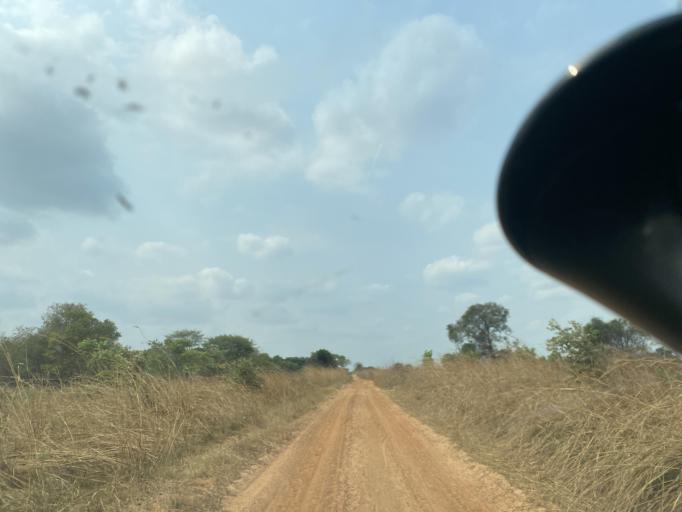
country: ZM
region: Lusaka
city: Lusaka
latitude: -15.1398
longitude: 28.3673
